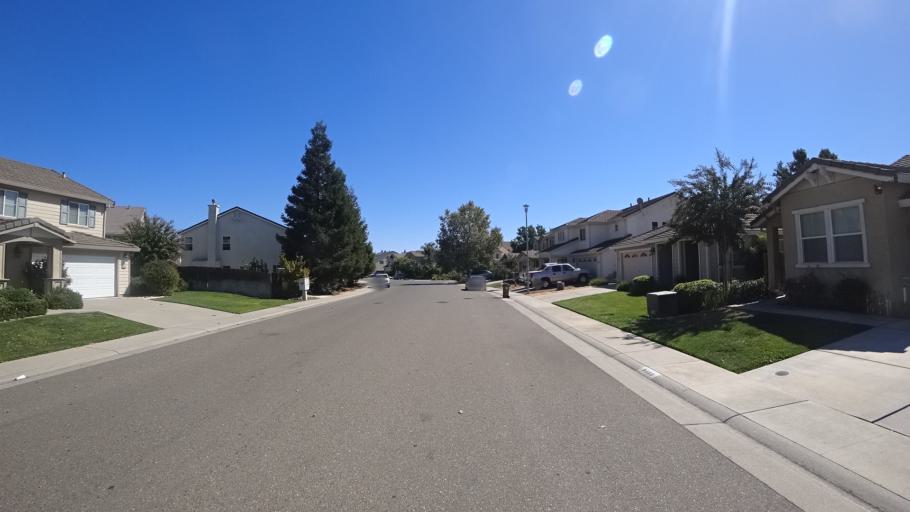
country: US
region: California
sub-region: Sacramento County
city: Elk Grove
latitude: 38.4192
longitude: -121.3469
